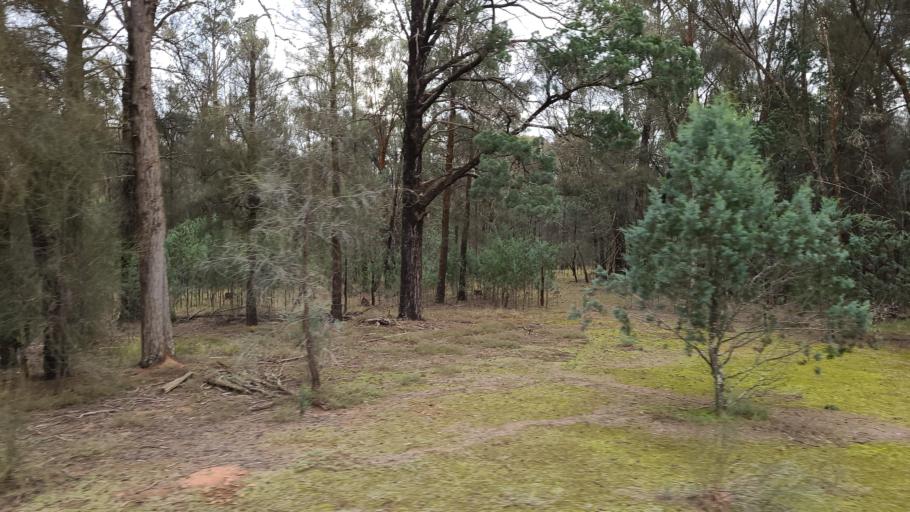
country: AU
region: New South Wales
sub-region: Coolamon
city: Coolamon
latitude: -34.8581
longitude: 146.9263
